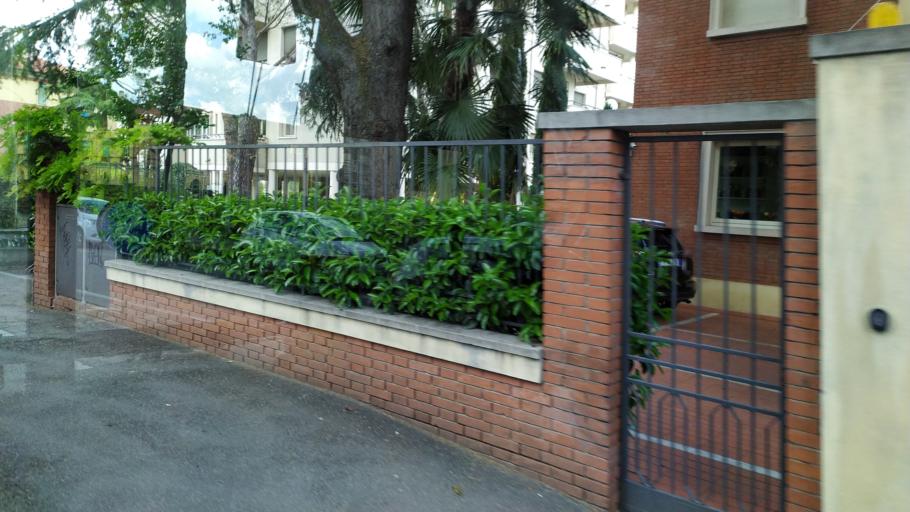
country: IT
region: Emilia-Romagna
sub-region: Provincia di Bologna
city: Imola
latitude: 44.3565
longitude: 11.7144
